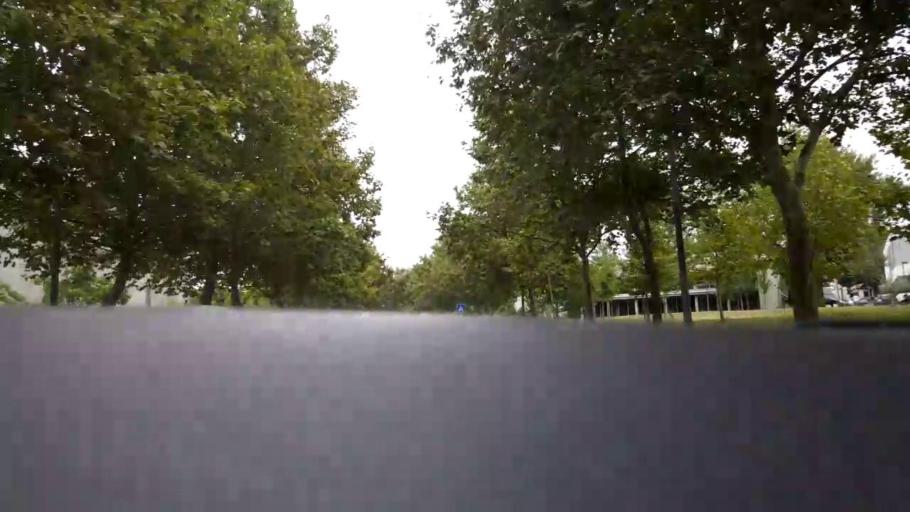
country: PT
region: Porto
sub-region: Maia
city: Pedroucos
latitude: 41.1772
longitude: -8.5967
